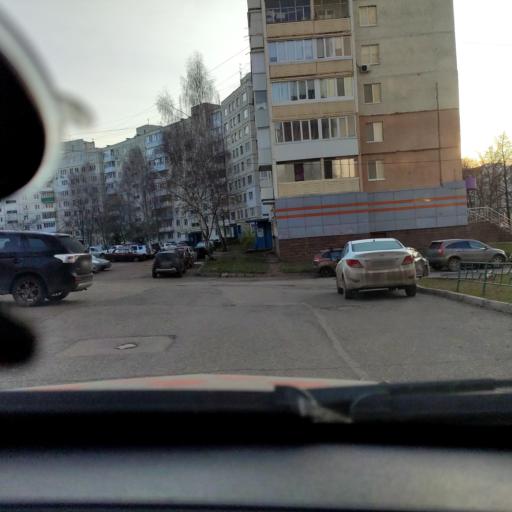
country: RU
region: Bashkortostan
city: Ufa
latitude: 54.6994
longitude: 55.9868
